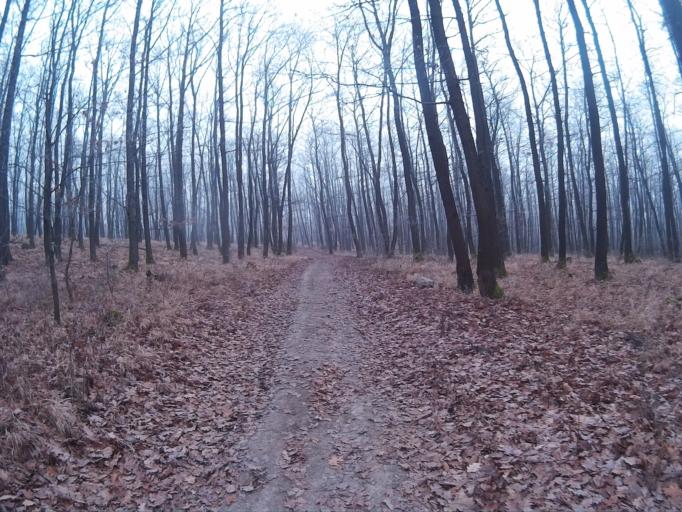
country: HU
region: Nograd
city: Rimoc
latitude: 47.9794
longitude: 19.5590
